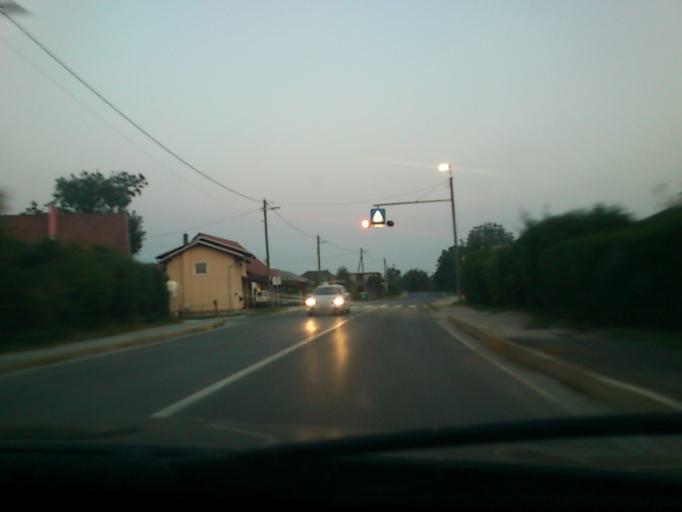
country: SI
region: Duplek
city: Spodnji Duplek
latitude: 46.4788
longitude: 15.7445
